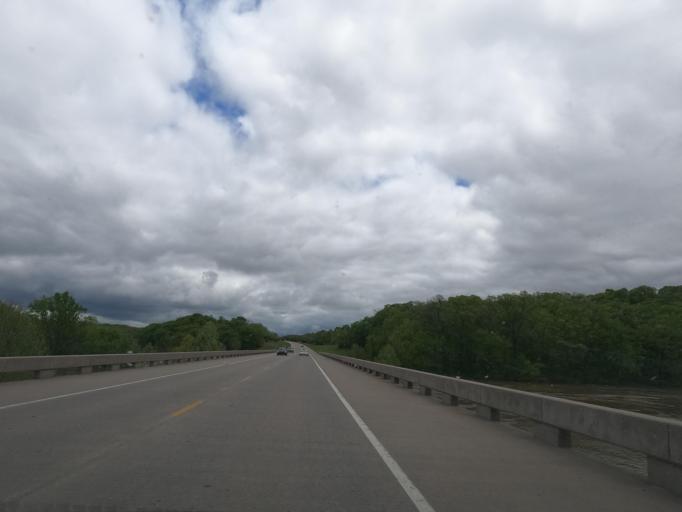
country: US
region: Kansas
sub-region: Wilson County
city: Neodesha
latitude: 37.3563
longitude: -95.6754
